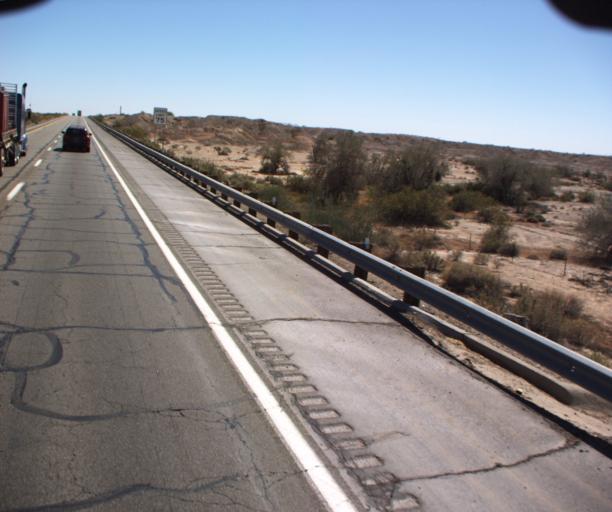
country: US
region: Arizona
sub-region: Yuma County
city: Wellton
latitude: 32.6627
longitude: -114.2667
